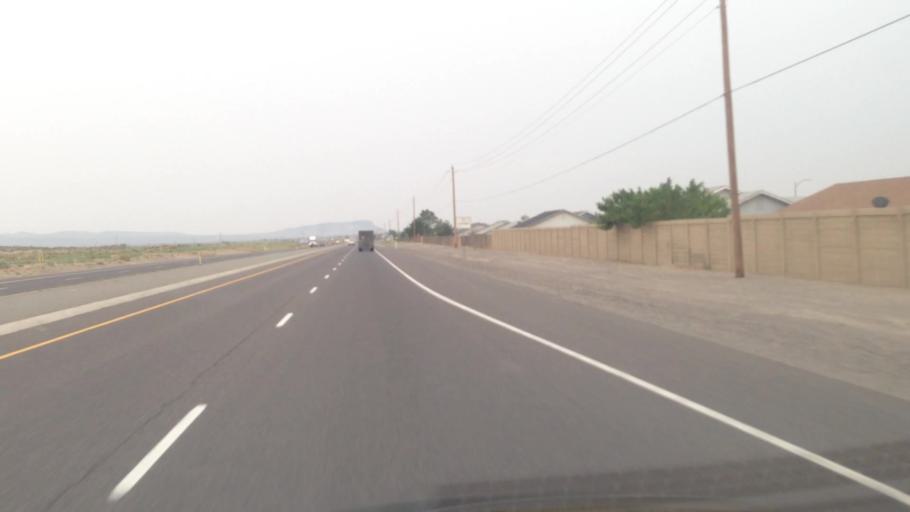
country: US
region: Nevada
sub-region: Lyon County
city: Fernley
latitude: 39.5995
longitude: -119.2063
